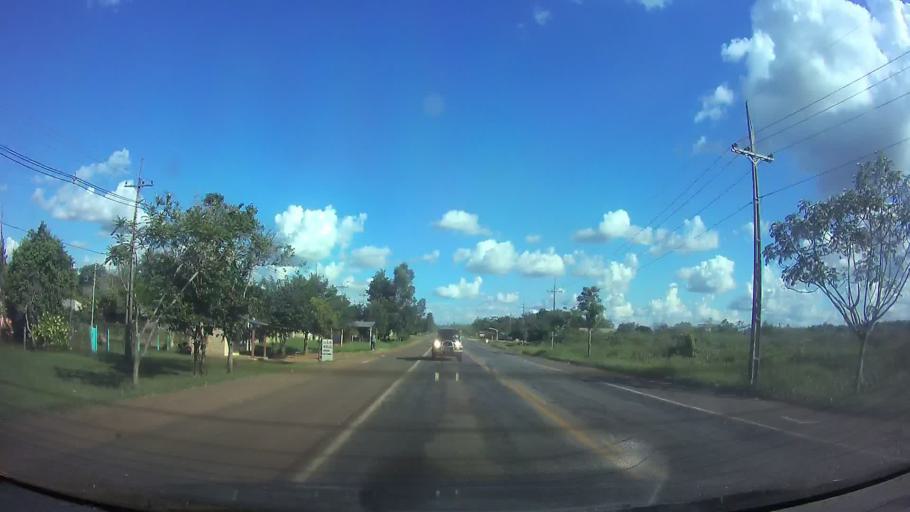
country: PY
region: Cordillera
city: Eusebio Ayala
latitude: -25.3853
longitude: -56.9700
